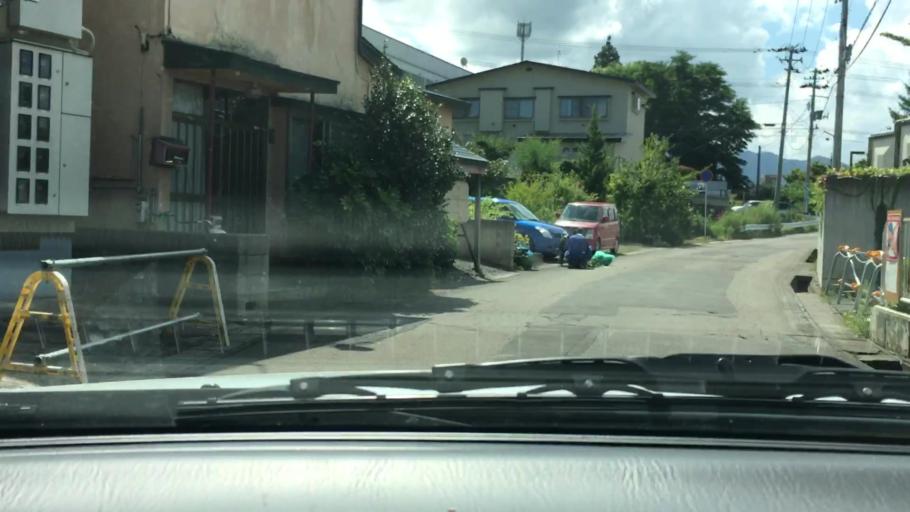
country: JP
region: Aomori
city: Hirosaki
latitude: 40.5866
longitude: 140.4675
